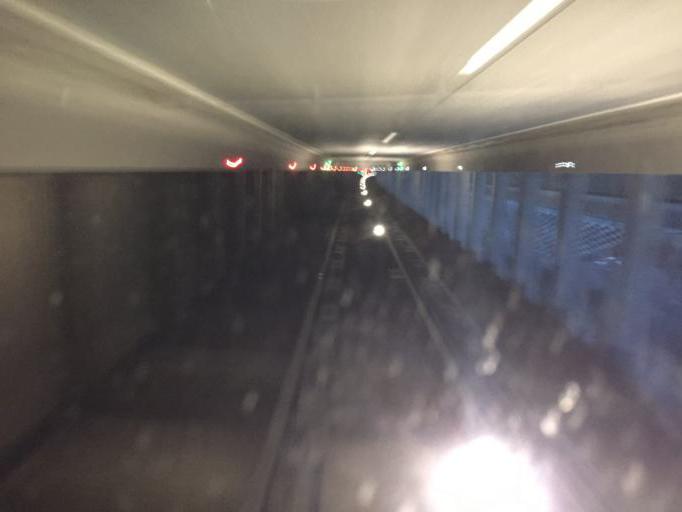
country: AT
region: Salzburg
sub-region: Politischer Bezirk Sankt Johann im Pongau
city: Eben im Pongau
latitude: 47.4014
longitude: 13.3947
